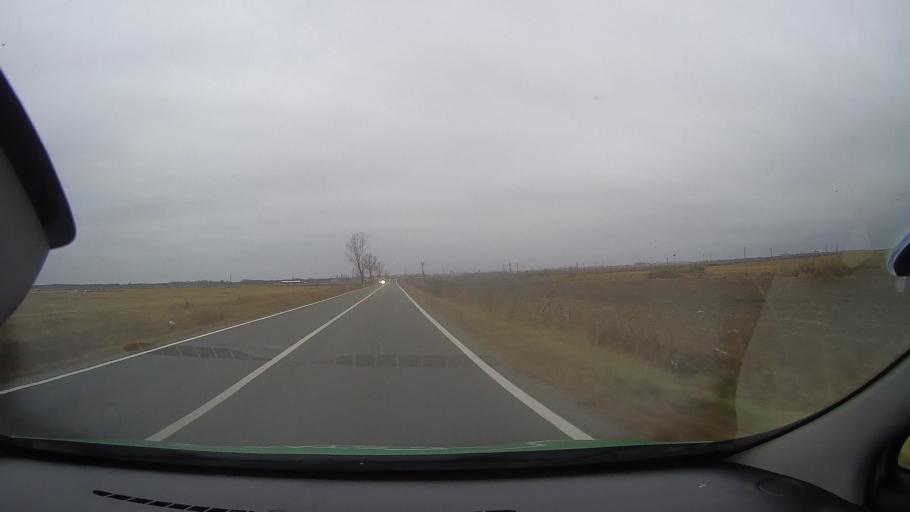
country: RO
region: Ialomita
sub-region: Comuna Slobozia
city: Slobozia
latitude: 44.5930
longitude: 27.3909
